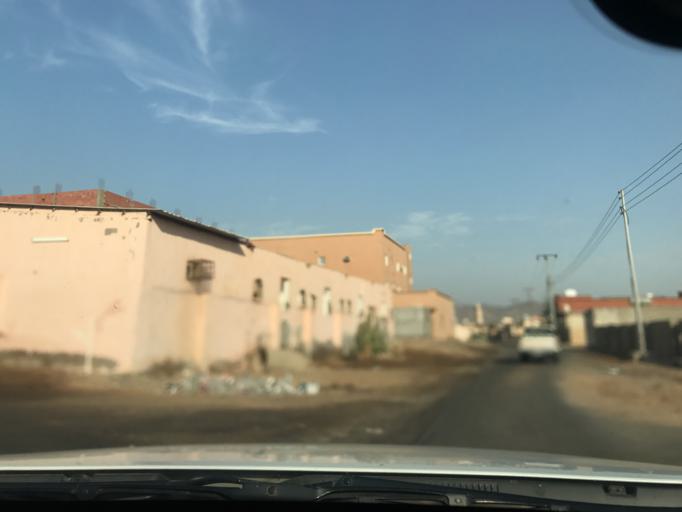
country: SA
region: Makkah
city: Al Jumum
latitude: 21.4421
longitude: 39.5199
